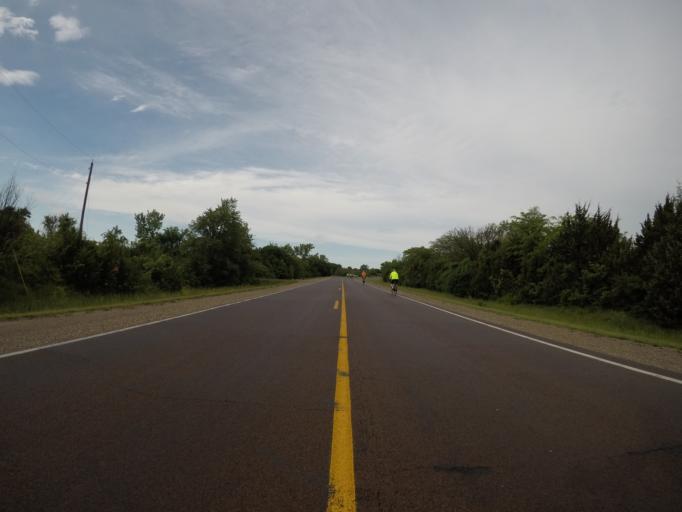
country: US
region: Kansas
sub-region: Shawnee County
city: Topeka
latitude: 38.9593
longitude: -95.7198
